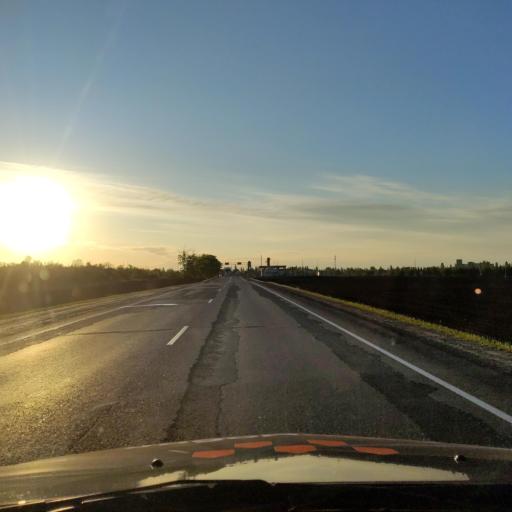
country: RU
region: Orjol
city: Livny
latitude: 52.4409
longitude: 37.5656
